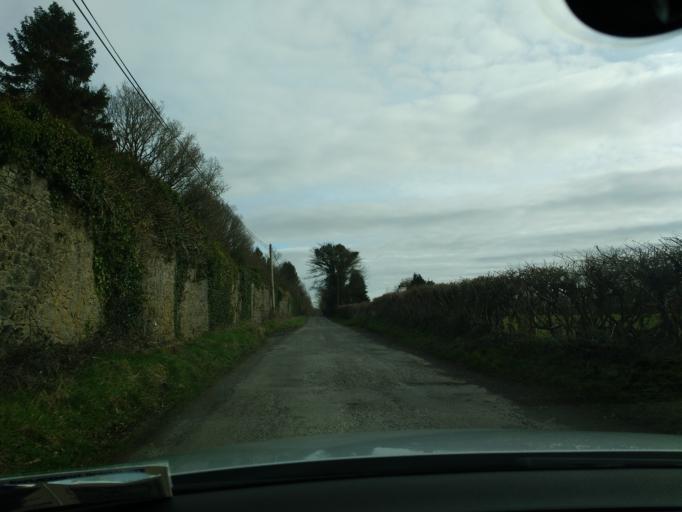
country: IE
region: Leinster
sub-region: Laois
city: Rathdowney
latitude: 52.6633
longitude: -7.5737
